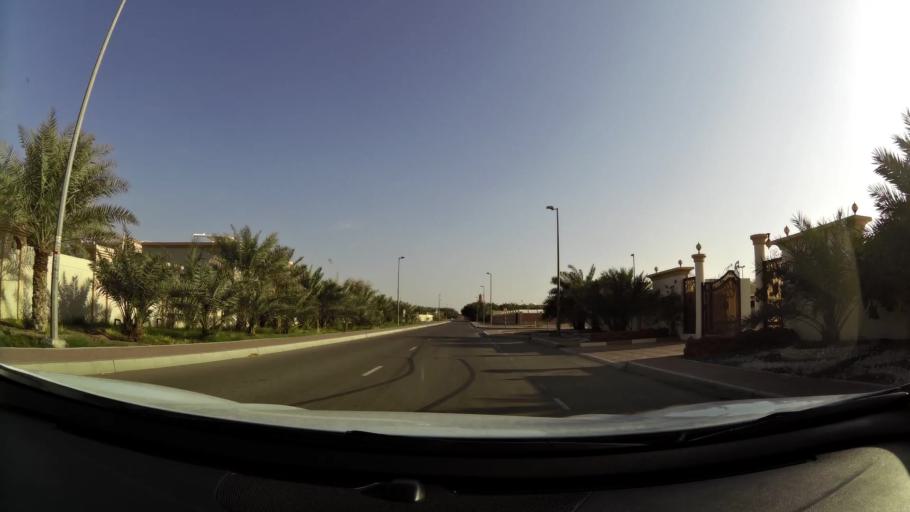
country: AE
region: Abu Dhabi
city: Al Ain
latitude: 24.0771
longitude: 55.8435
